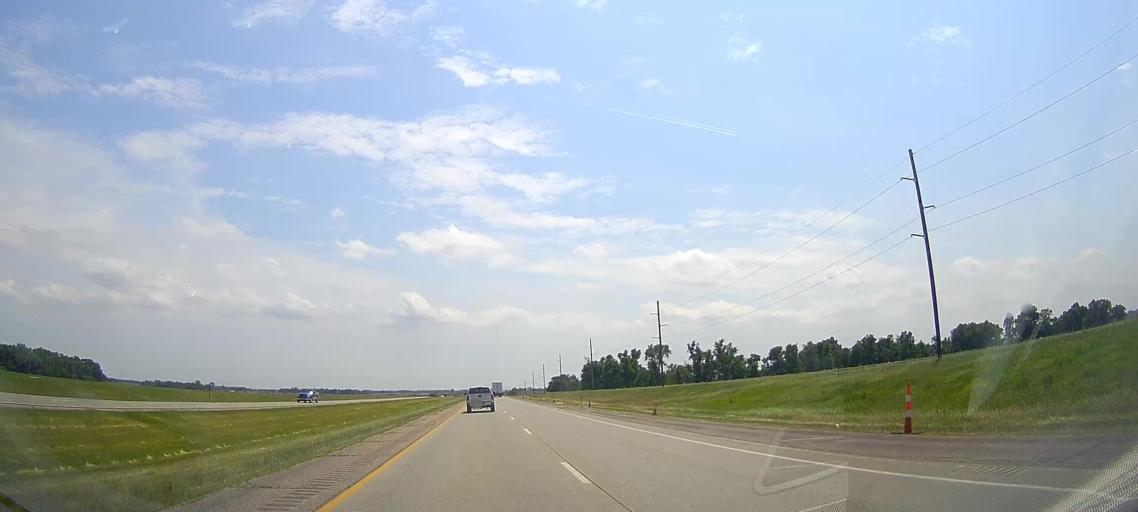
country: US
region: South Dakota
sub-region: Lincoln County
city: Tea
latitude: 43.3777
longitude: -96.7965
